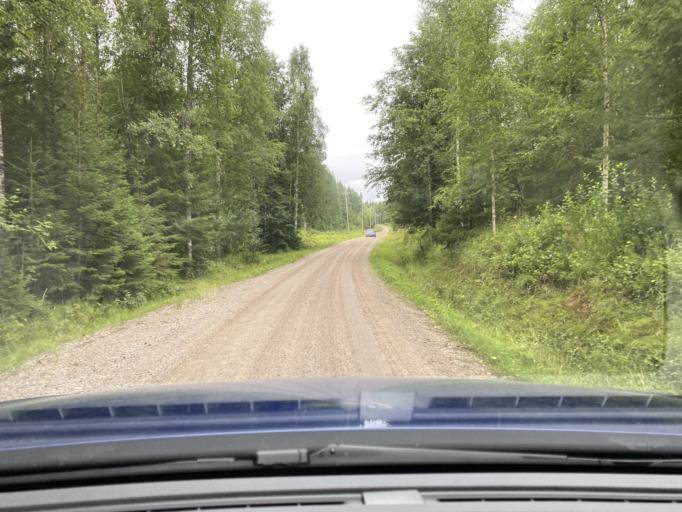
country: FI
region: Pirkanmaa
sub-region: Ylae-Pirkanmaa
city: Maenttae
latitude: 62.0198
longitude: 24.7375
